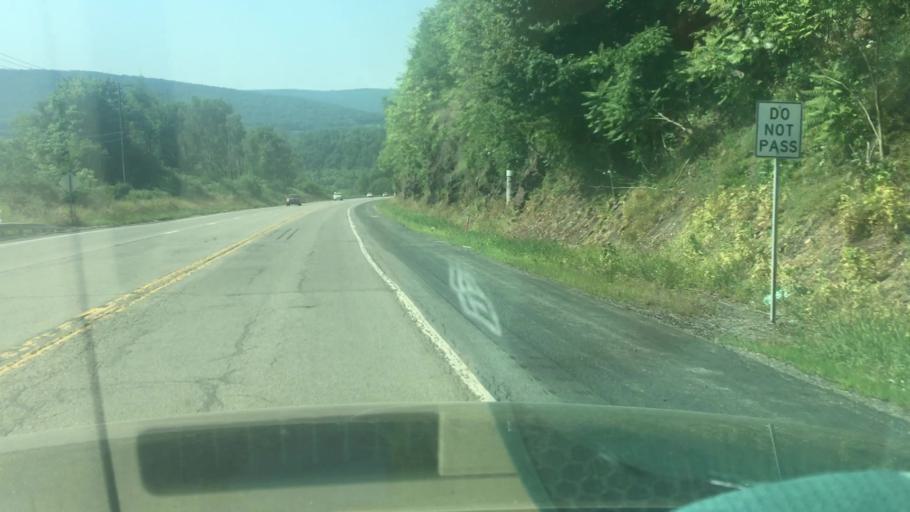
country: US
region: Pennsylvania
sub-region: Schuylkill County
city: Ashland
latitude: 40.7559
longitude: -76.3826
